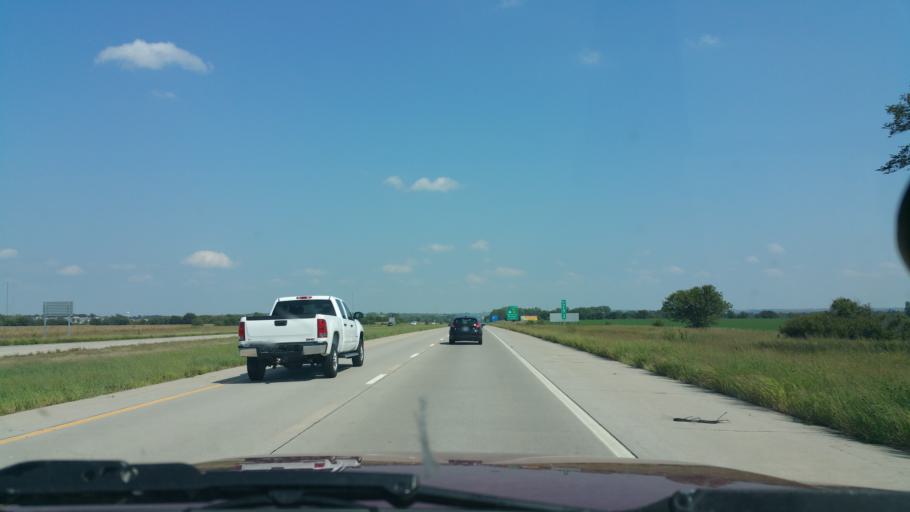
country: US
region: Kansas
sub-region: Geary County
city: Junction City
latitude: 39.0007
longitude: -96.8996
